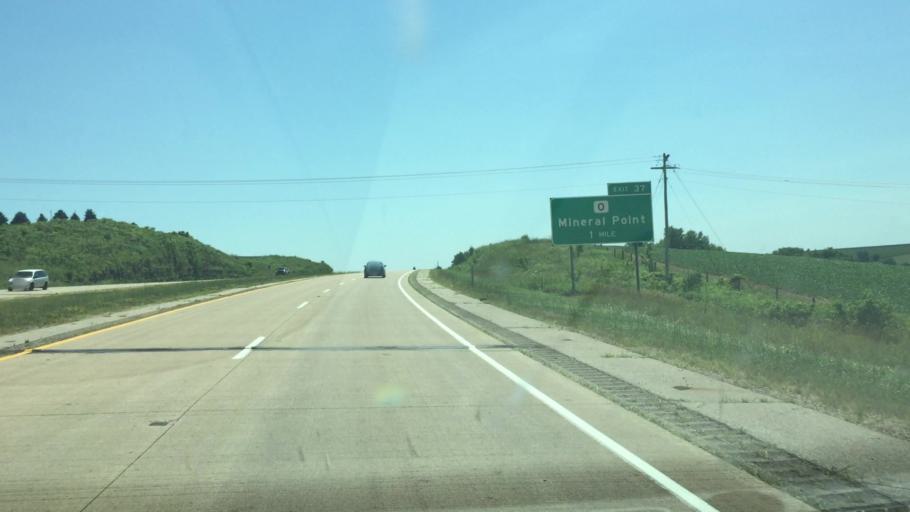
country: US
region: Wisconsin
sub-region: Iowa County
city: Mineral Point
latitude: 42.8668
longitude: -90.1964
